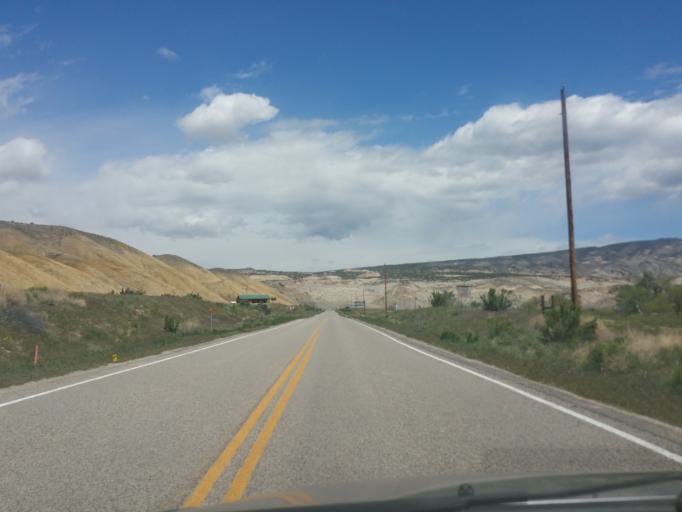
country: US
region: Utah
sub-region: Uintah County
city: Naples
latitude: 40.4199
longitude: -109.3378
